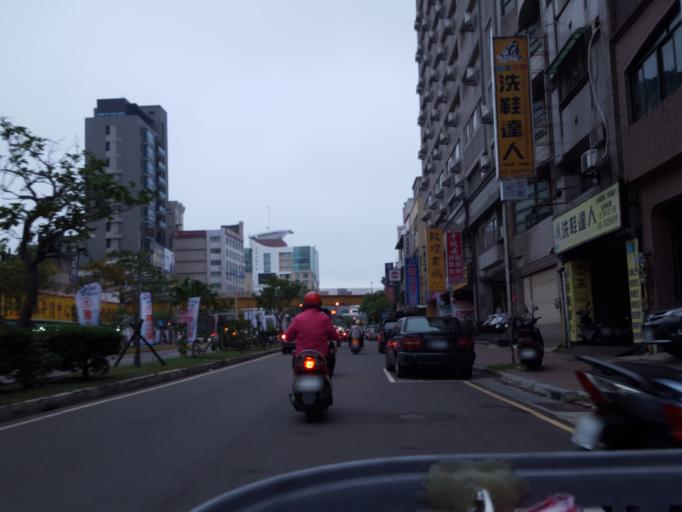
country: TW
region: Taiwan
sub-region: Hsinchu
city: Hsinchu
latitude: 24.8154
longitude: 120.9659
